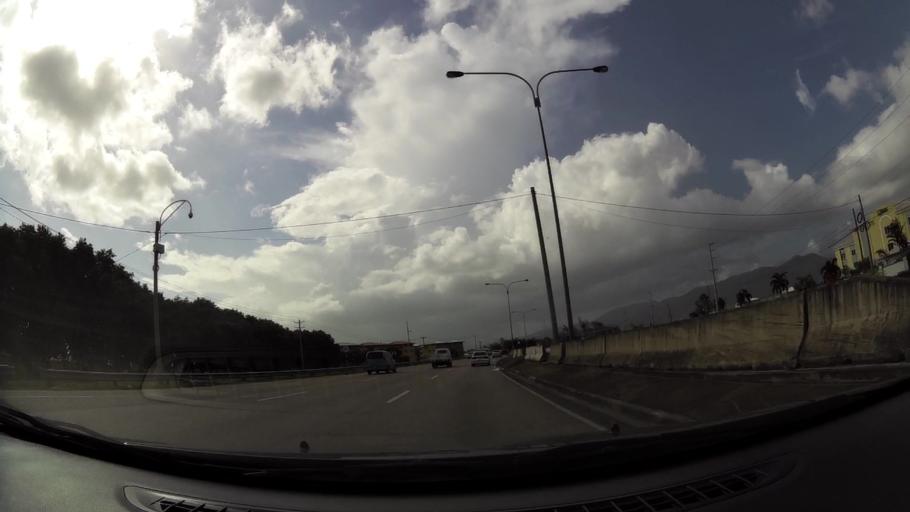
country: TT
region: Tunapuna/Piarco
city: Arouca
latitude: 10.6174
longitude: -61.3497
